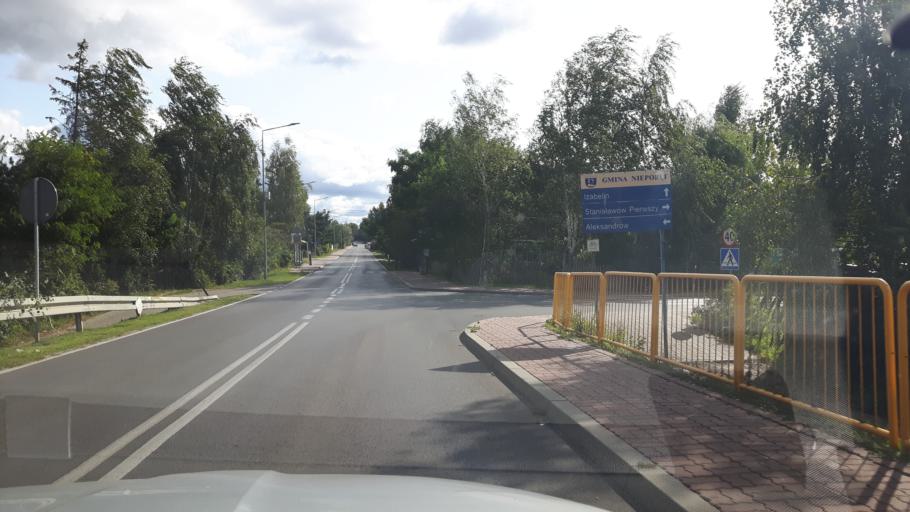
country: PL
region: Masovian Voivodeship
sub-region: Powiat legionowski
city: Stanislawow Pierwszy
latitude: 52.3967
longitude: 21.0438
